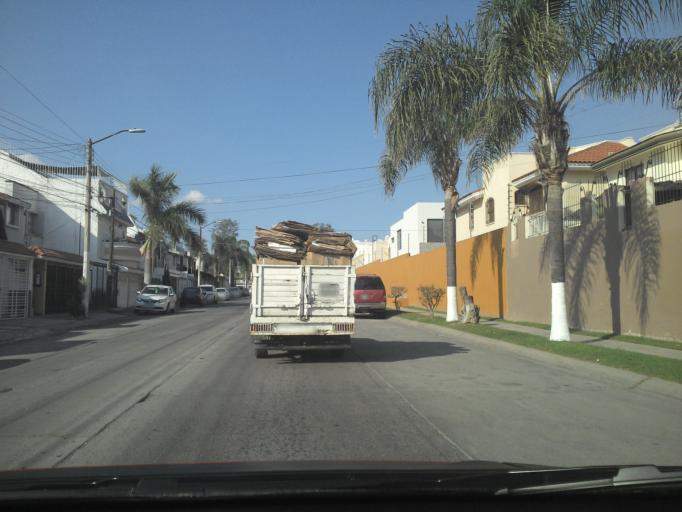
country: MX
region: Jalisco
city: Guadalajara
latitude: 20.6574
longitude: -103.4426
